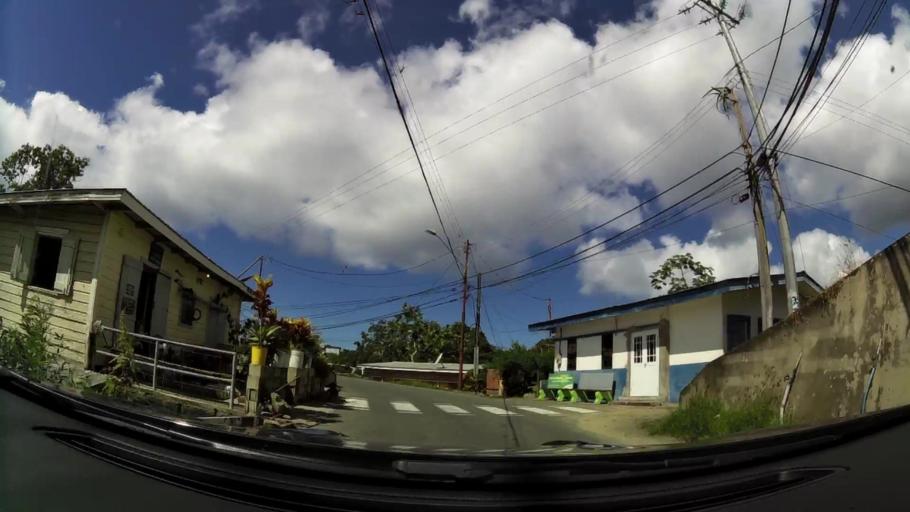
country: TT
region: Tobago
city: Scarborough
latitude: 11.2488
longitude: -60.7166
